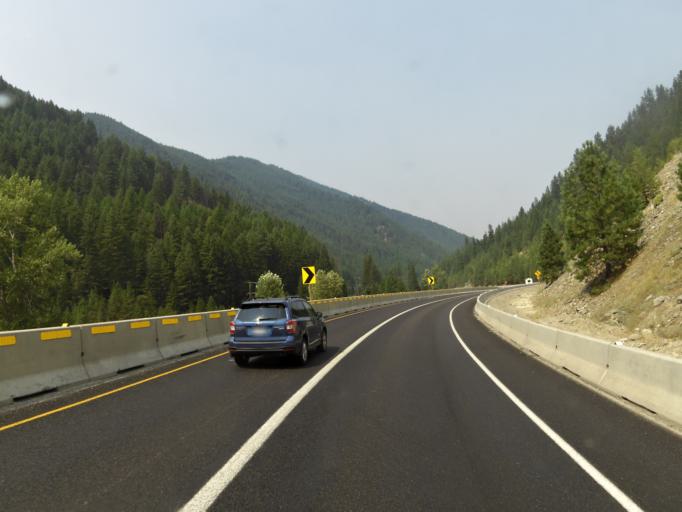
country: US
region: Montana
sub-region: Sanders County
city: Thompson Falls
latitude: 47.3131
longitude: -115.2340
